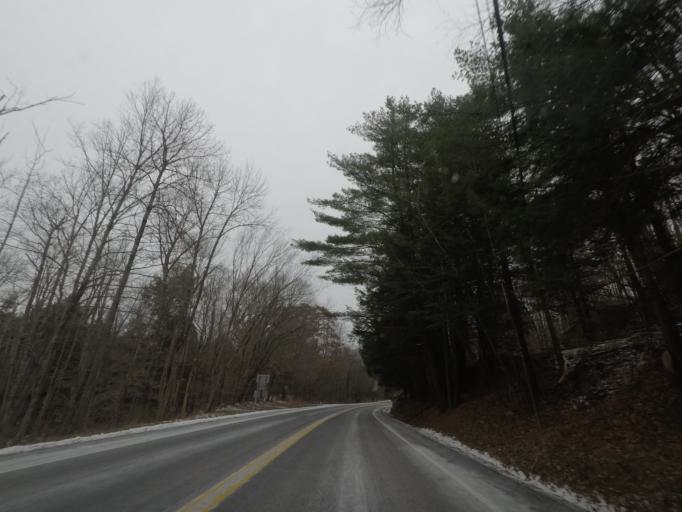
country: US
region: New York
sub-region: Rensselaer County
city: Hoosick Falls
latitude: 42.7634
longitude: -73.3921
